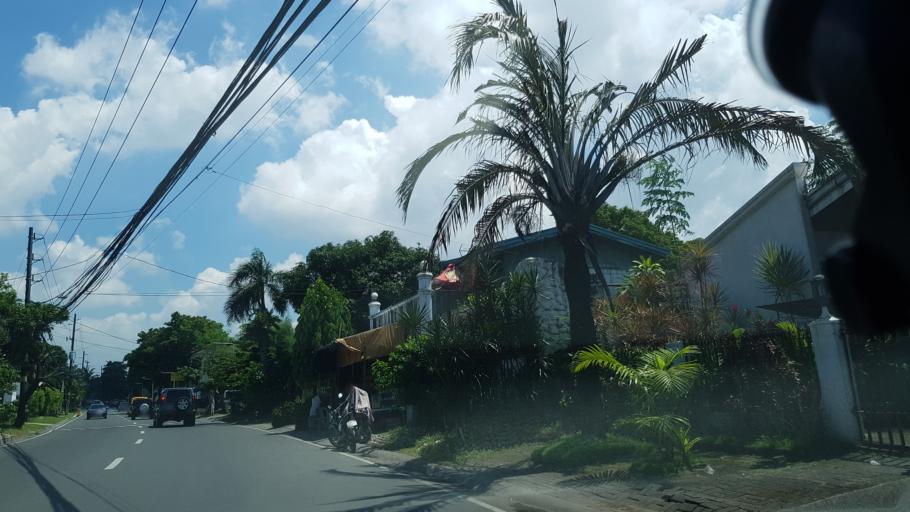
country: PH
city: Sambayanihan People's Village
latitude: 14.4520
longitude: 120.9975
